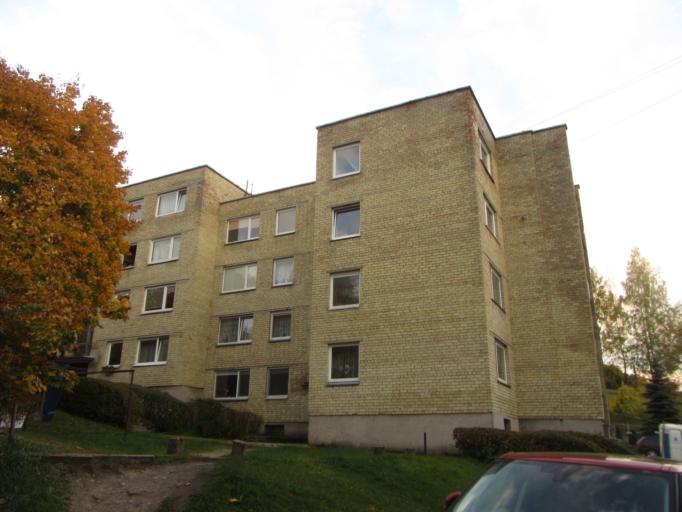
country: LT
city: Trakai
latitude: 54.6356
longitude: 24.9365
